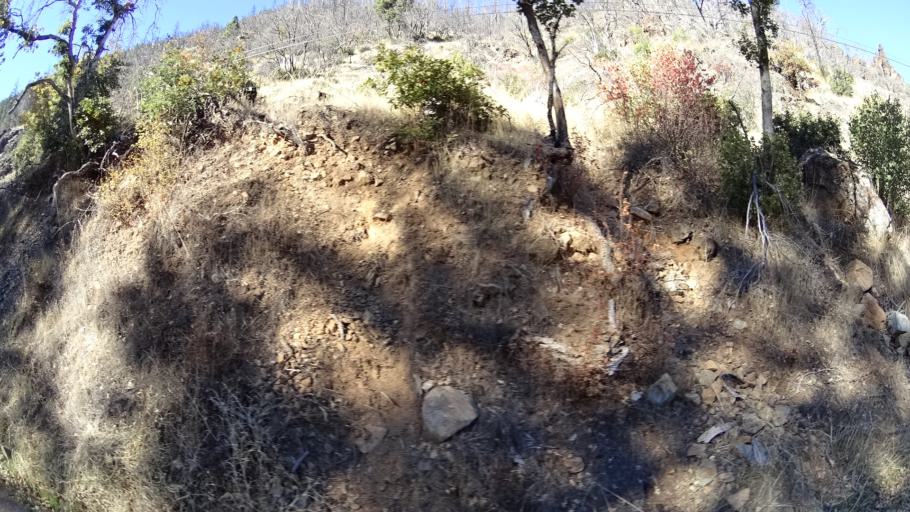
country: US
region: California
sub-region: Siskiyou County
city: Happy Camp
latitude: 41.2997
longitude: -123.0803
